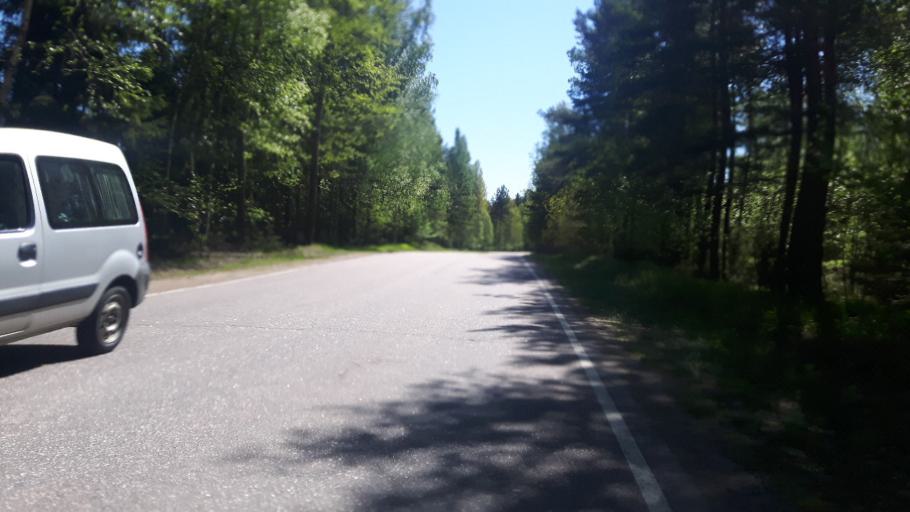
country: RU
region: Leningrad
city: Glebychevo
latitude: 60.3427
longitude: 28.8225
